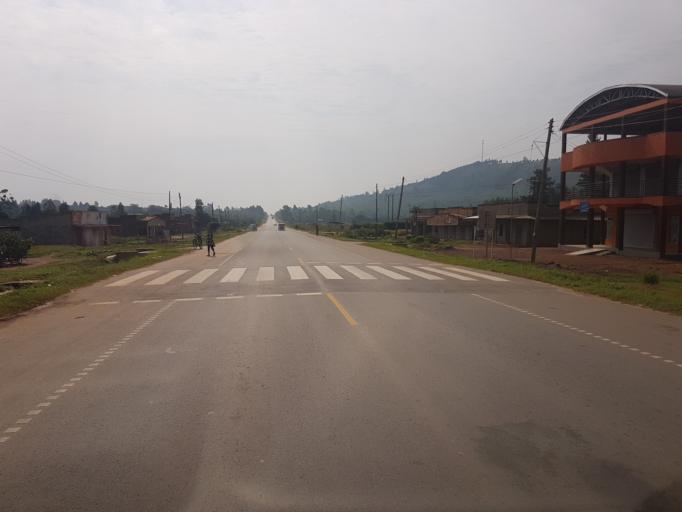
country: UG
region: Western Region
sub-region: Sheema District
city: Kibingo
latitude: -0.6420
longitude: 30.5033
